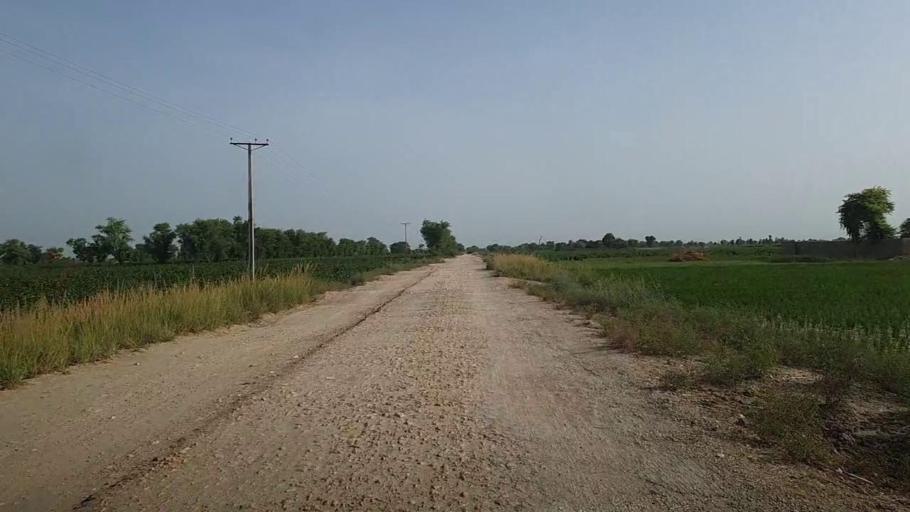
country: PK
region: Sindh
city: Pad Idan
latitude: 26.7645
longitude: 68.2572
